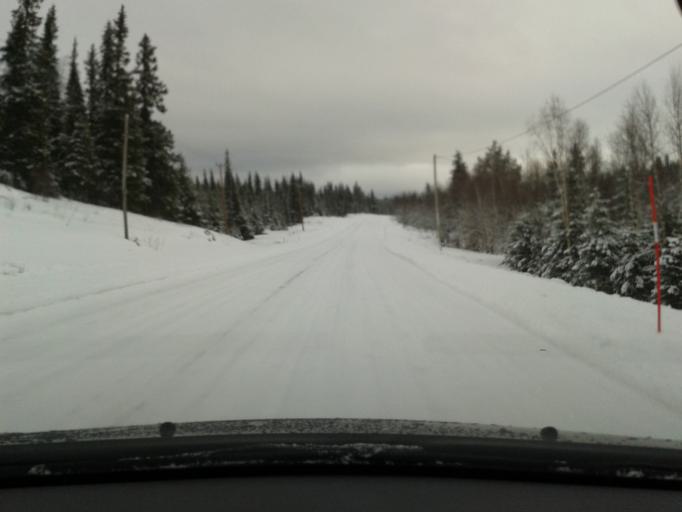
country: SE
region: Vaesterbotten
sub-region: Vilhelmina Kommun
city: Sjoberg
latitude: 65.2425
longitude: 15.7628
